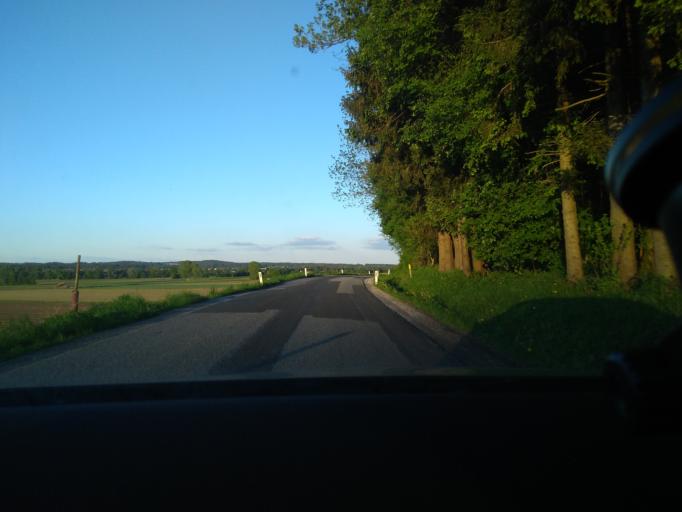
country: AT
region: Styria
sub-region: Politischer Bezirk Voitsberg
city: Mooskirchen
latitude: 46.9739
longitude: 15.2867
